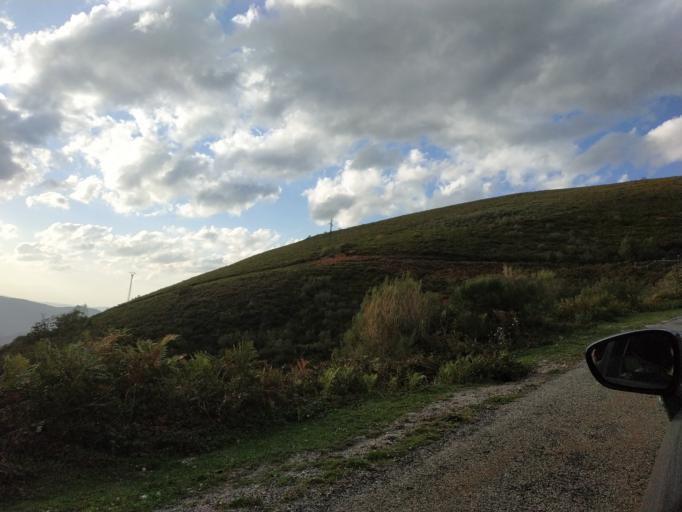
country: ES
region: Castille and Leon
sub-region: Provincia de Leon
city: Candin
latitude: 42.8696
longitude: -6.8353
